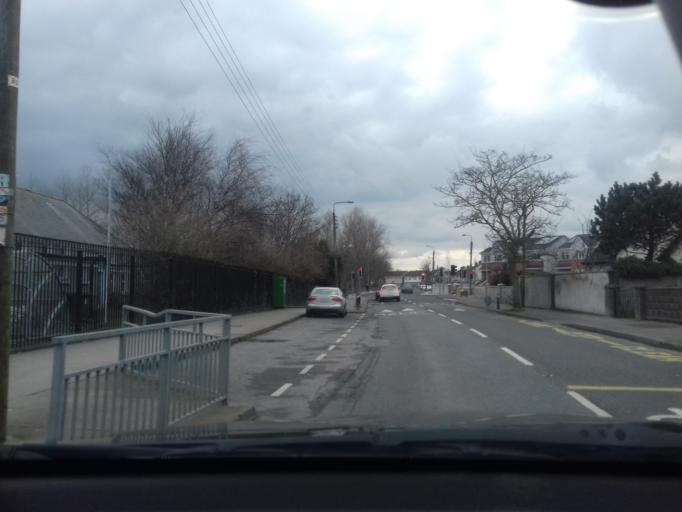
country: IE
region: Leinster
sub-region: Fingal County
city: Baldoyle
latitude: 53.3968
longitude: -6.1328
